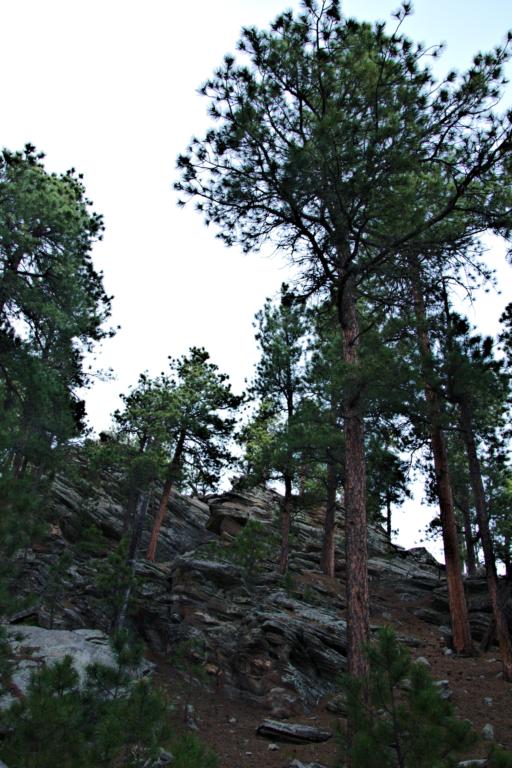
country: US
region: South Dakota
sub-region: Custer County
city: Custer
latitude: 43.8788
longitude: -103.4563
